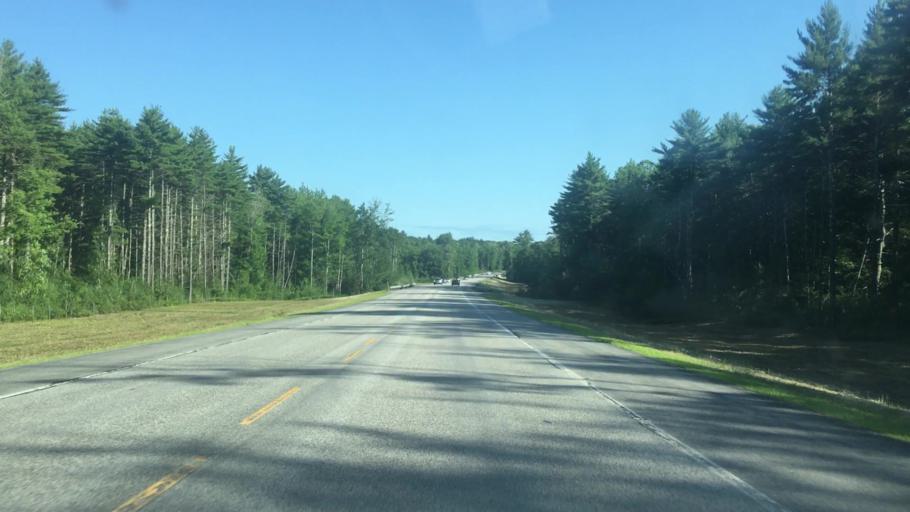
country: US
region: Maine
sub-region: Cumberland County
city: Gorham
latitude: 43.6617
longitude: -70.4511
